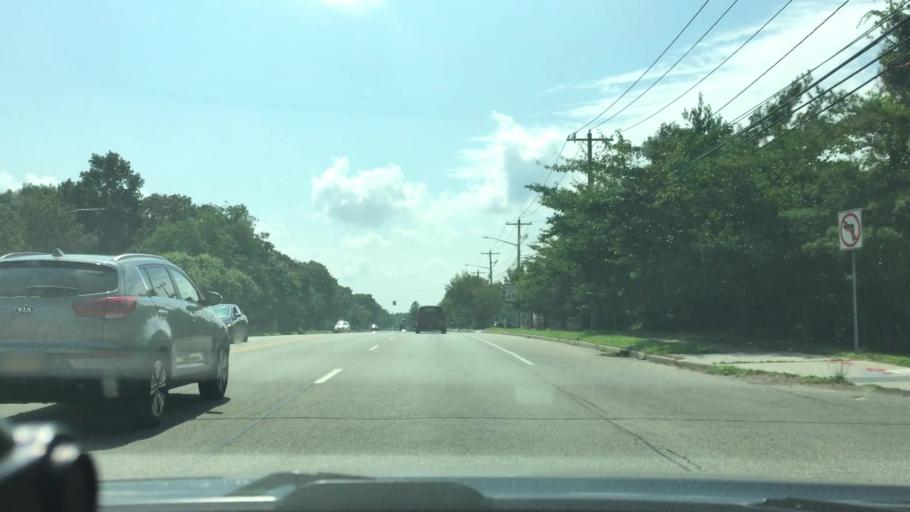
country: US
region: New York
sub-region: Suffolk County
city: Mount Sinai
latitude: 40.9339
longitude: -73.0261
